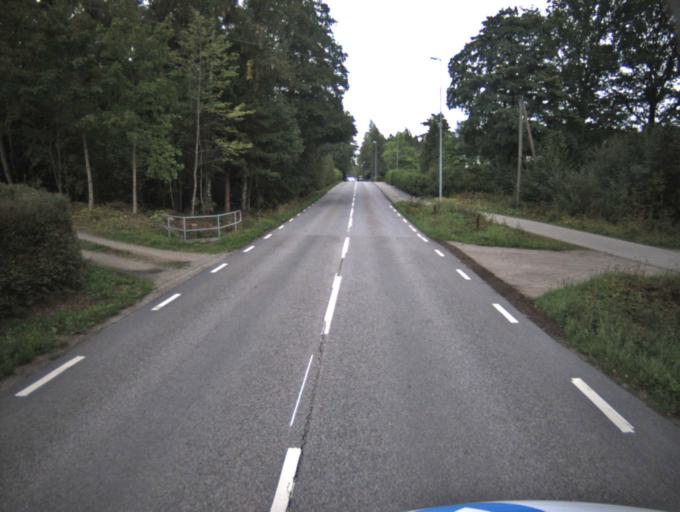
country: SE
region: Vaestra Goetaland
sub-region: Ulricehamns Kommun
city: Ulricehamn
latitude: 57.7772
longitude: 13.4267
